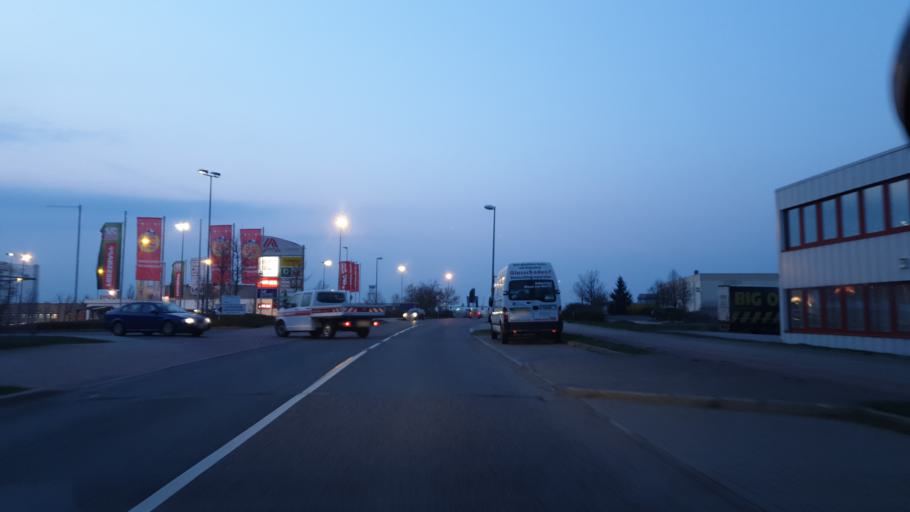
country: DE
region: Saxony
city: Stollberg
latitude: 50.7054
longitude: 12.7596
